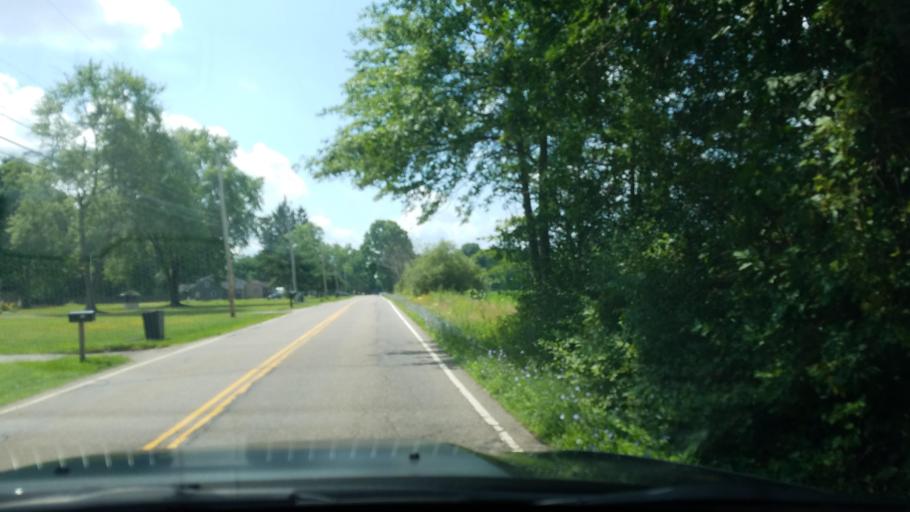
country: US
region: Ohio
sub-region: Trumbull County
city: Champion Heights
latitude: 41.2762
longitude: -80.8675
